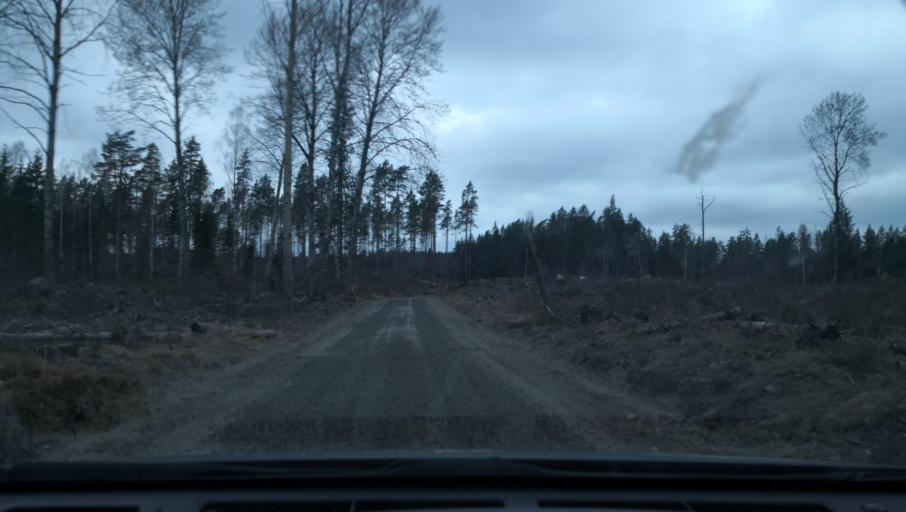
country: SE
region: OErebro
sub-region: Lindesbergs Kommun
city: Fellingsbro
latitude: 59.6132
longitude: 15.5981
